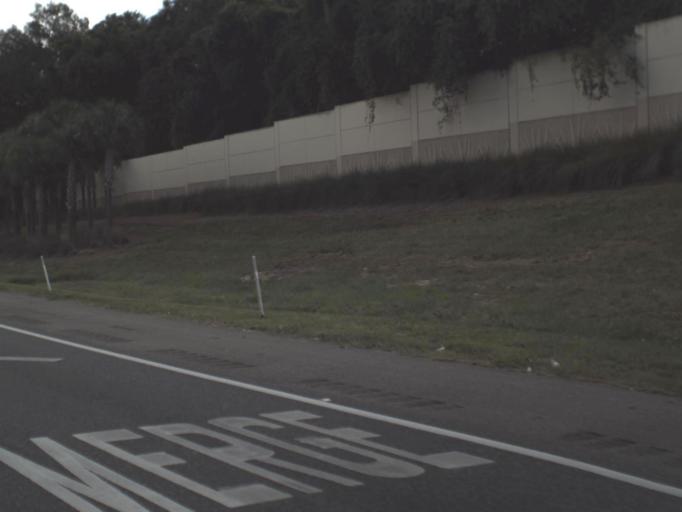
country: US
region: Florida
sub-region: Orange County
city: Oakland
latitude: 28.5482
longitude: -81.6274
